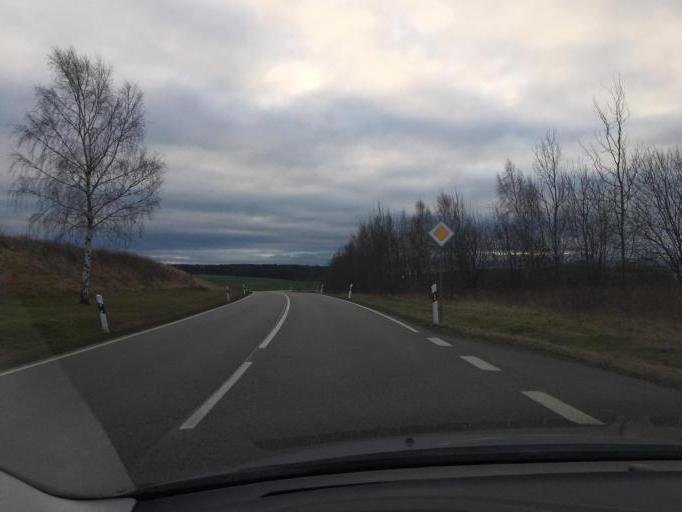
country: DE
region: Thuringia
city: Langenleuba-Niederhain
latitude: 50.9901
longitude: 12.6053
